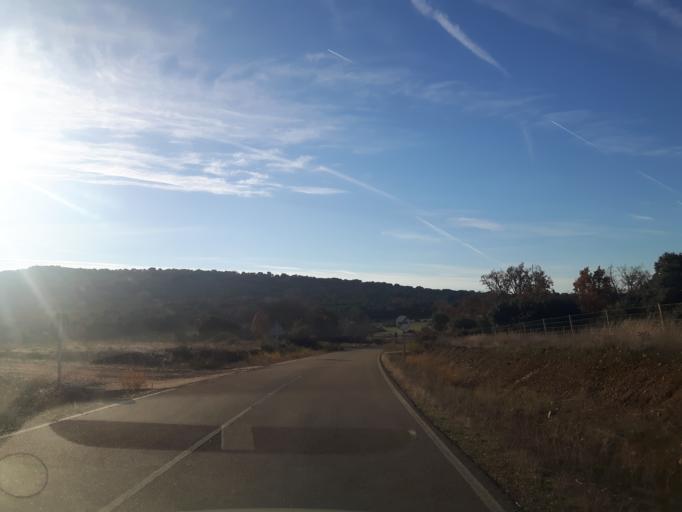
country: ES
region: Castille and Leon
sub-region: Provincia de Salamanca
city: Olmedo de Camaces
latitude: 40.9073
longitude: -6.6183
